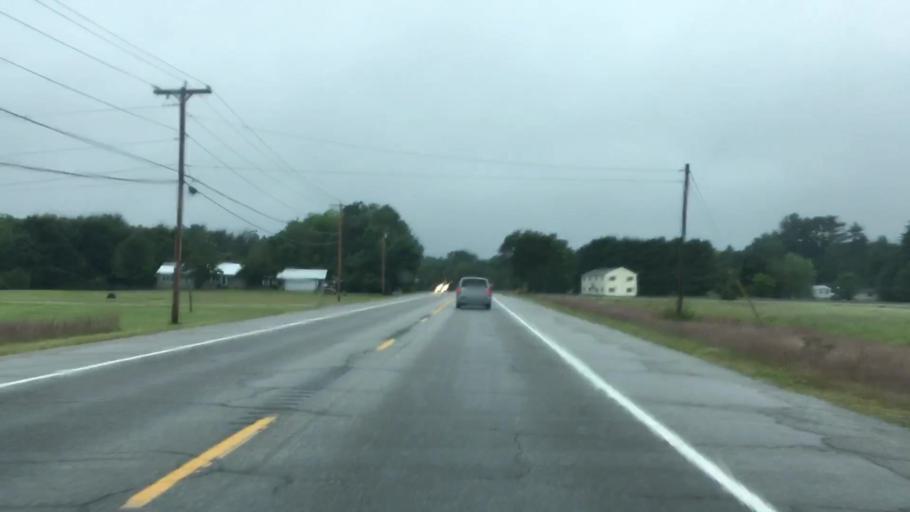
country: US
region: Maine
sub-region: Cumberland County
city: Raymond
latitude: 43.9564
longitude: -70.5597
